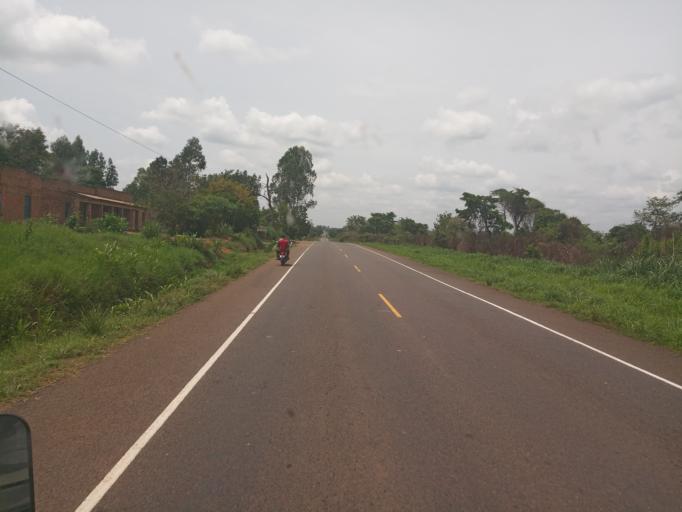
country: UG
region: Northern Region
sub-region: Oyam District
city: Oyam
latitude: 2.1763
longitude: 32.2240
